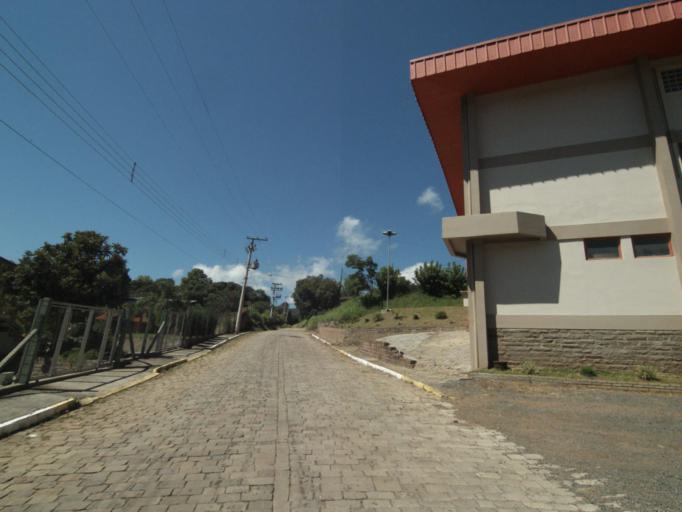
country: BR
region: Rio Grande do Sul
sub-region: Bento Goncalves
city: Bento Goncalves
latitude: -29.0936
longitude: -51.6281
